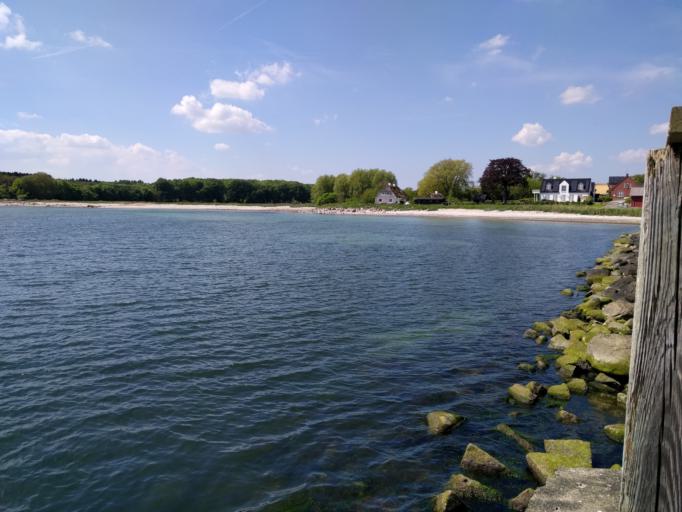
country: DK
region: Zealand
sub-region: Guldborgsund Kommune
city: Stubbekobing
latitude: 54.8226
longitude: 12.1380
